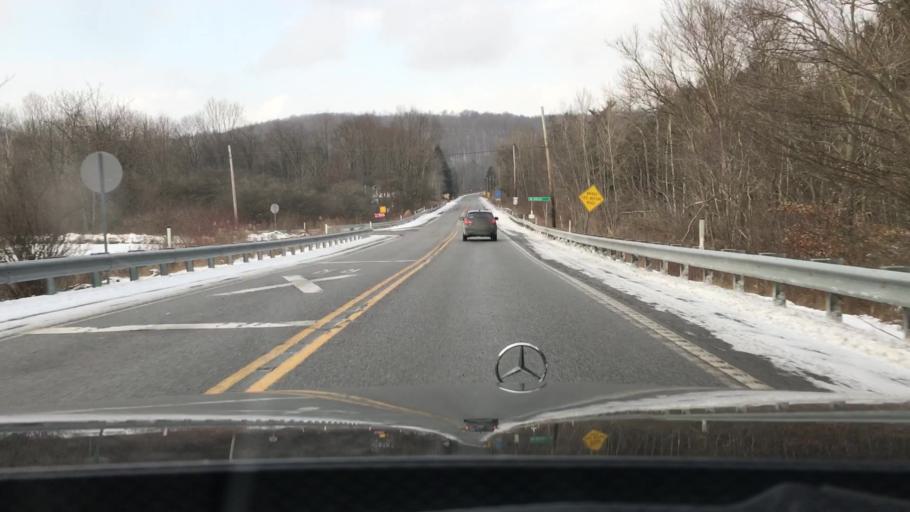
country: US
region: Pennsylvania
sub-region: Cambria County
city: Gallitzin
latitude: 40.5078
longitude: -78.5818
